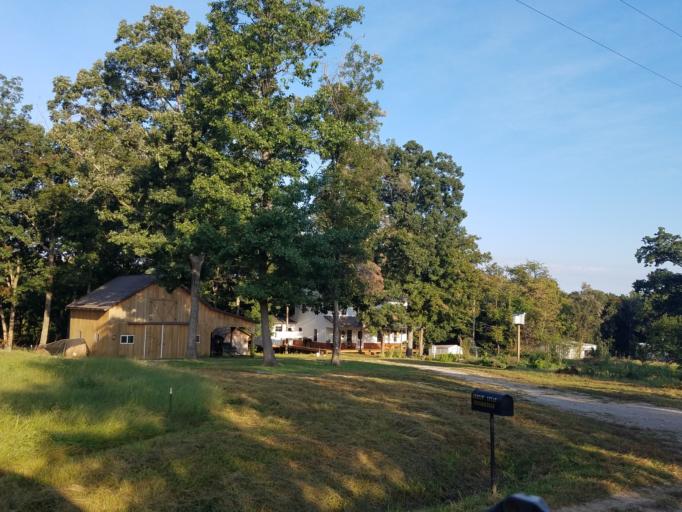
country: US
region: Missouri
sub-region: Moniteau County
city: California
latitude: 38.7479
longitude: -92.6428
